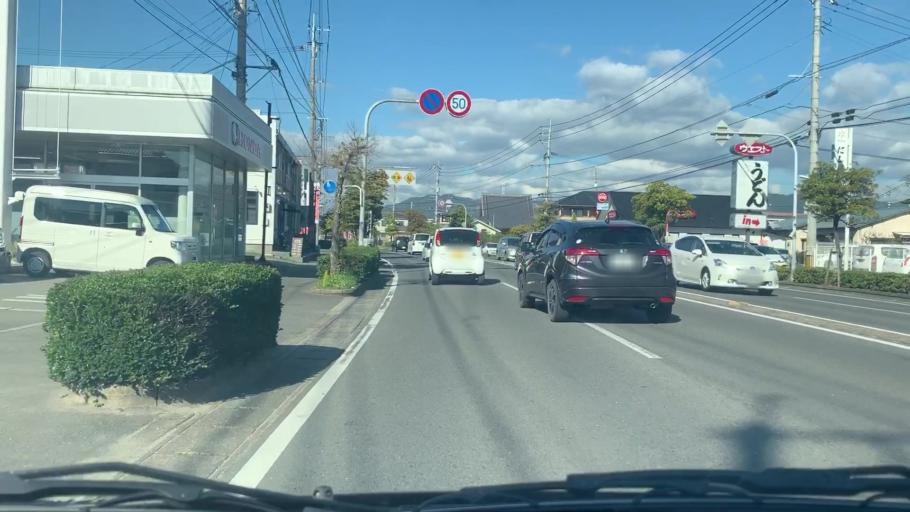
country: JP
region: Saga Prefecture
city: Saga-shi
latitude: 33.2831
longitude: 130.2918
